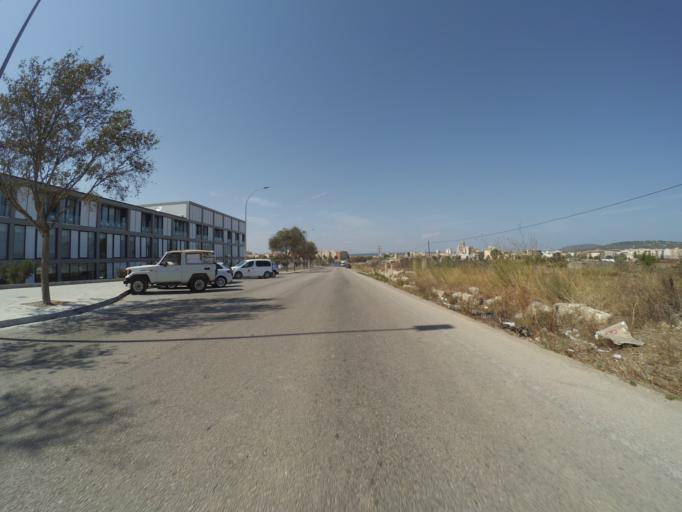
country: ES
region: Balearic Islands
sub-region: Illes Balears
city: Manacor
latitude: 39.5597
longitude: 3.2157
